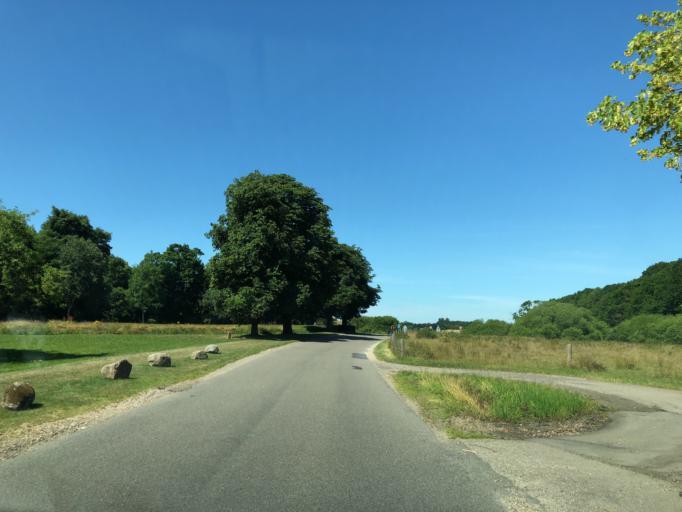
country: DK
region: Central Jutland
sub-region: Holstebro Kommune
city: Holstebro
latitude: 56.3505
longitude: 8.6869
